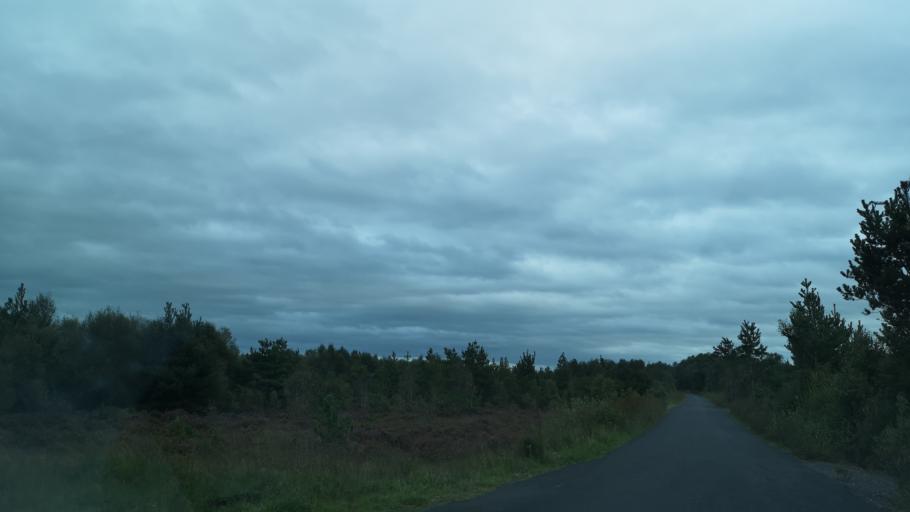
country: IE
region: Leinster
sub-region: Uibh Fhaili
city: Ferbane
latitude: 53.2047
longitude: -7.7244
